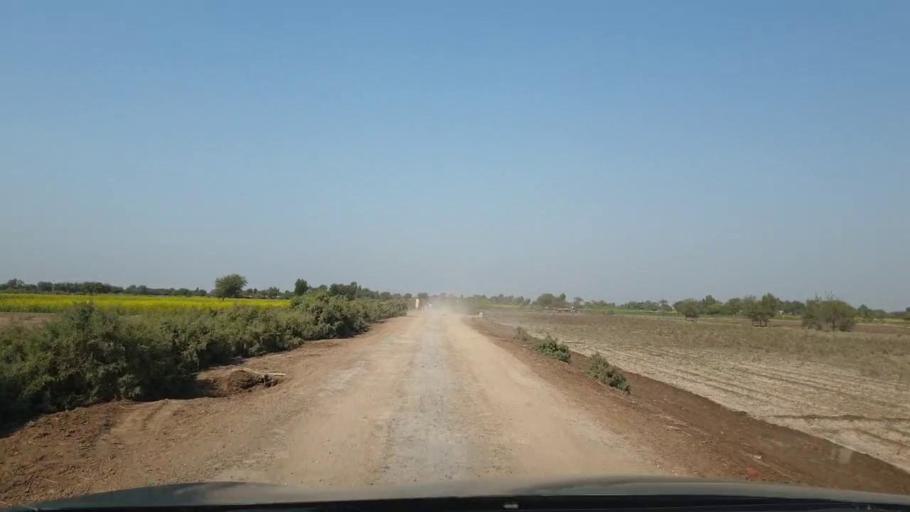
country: PK
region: Sindh
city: Berani
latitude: 25.6231
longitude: 68.8454
